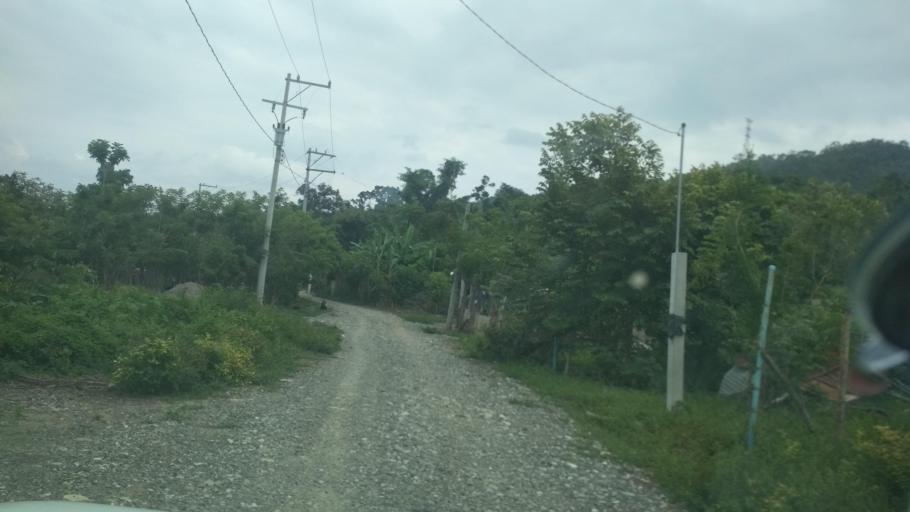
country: MX
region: Veracruz
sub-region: Poza Rica de Hidalgo
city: El Mollejon
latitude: 20.5342
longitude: -97.3903
